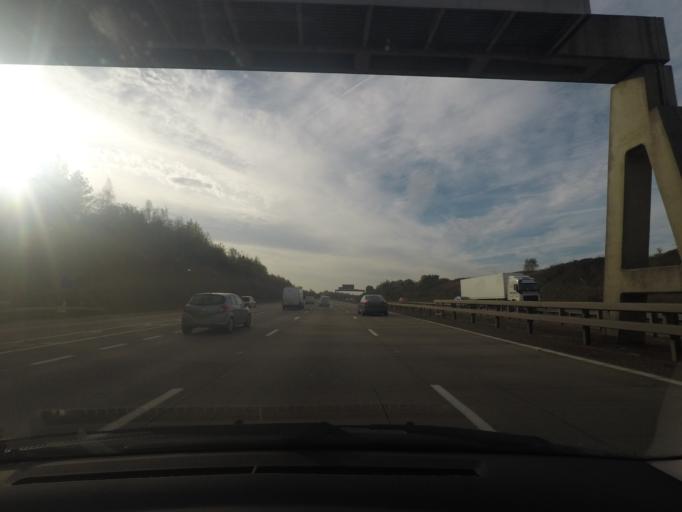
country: GB
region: England
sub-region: City and Borough of Leeds
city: Swillington
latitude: 53.7859
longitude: -1.4280
